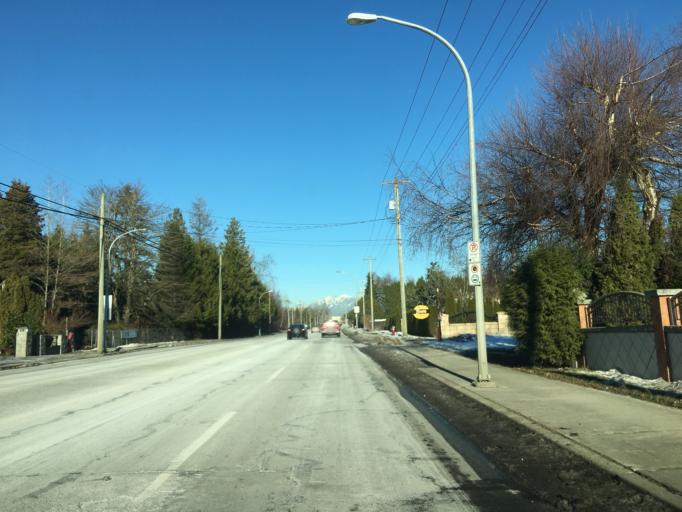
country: CA
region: British Columbia
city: Richmond
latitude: 49.1633
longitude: -123.0916
